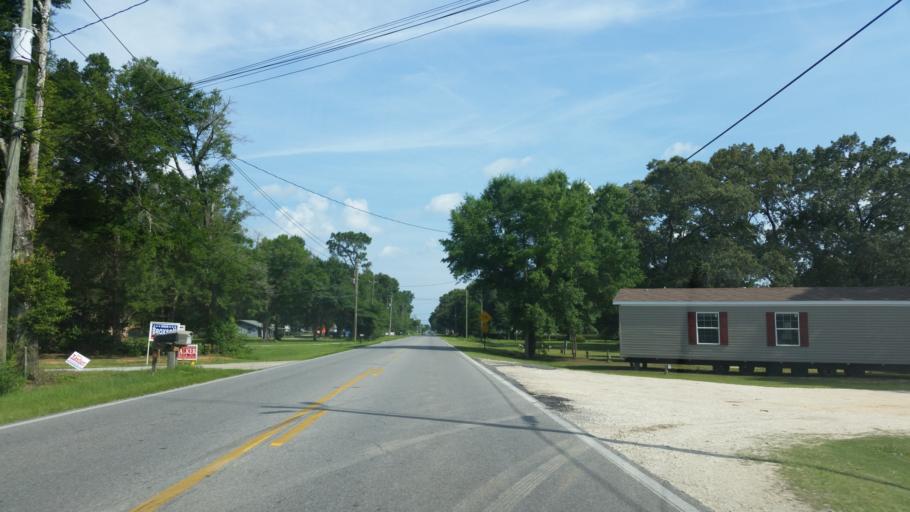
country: US
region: Florida
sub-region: Escambia County
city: Ensley
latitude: 30.5463
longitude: -87.2806
